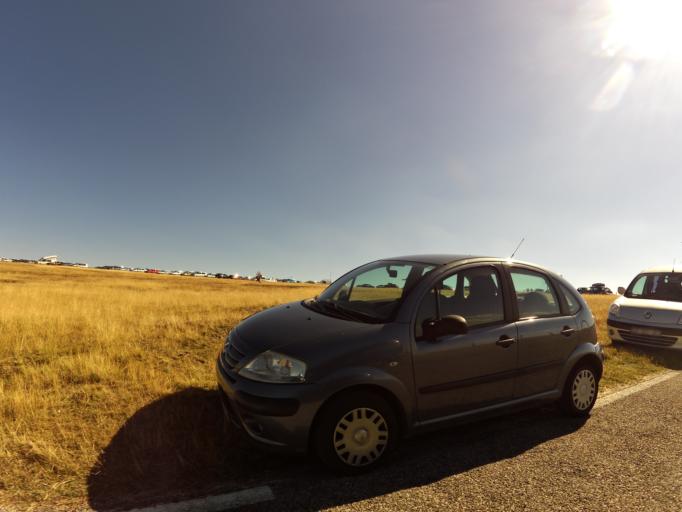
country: FR
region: Languedoc-Roussillon
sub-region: Departement du Gard
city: Valleraugue
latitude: 44.1222
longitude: 3.5777
